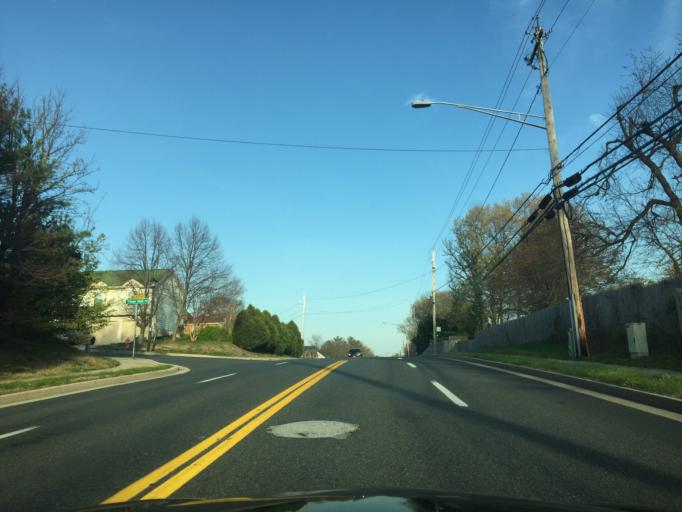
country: US
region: Maryland
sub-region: Baltimore County
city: Perry Hall
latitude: 39.3868
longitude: -76.4659
